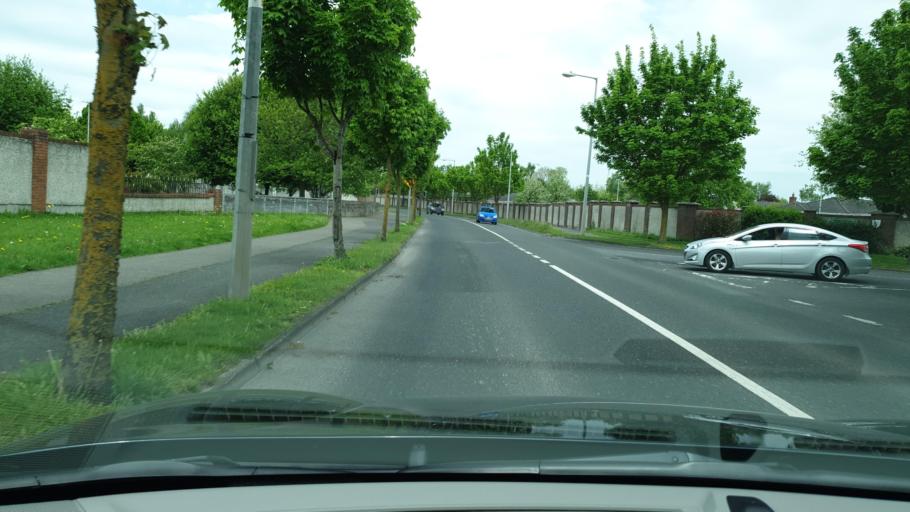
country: IE
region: Leinster
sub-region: Kildare
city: Clane
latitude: 53.2928
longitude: -6.6801
